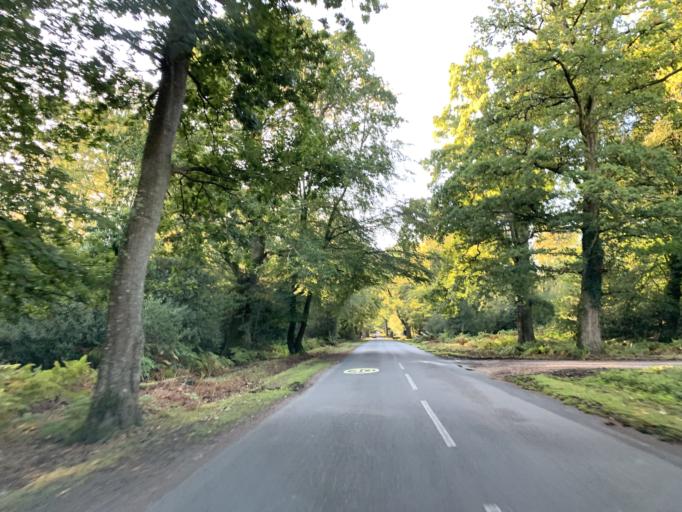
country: GB
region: England
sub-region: Hampshire
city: West Wellow
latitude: 50.9570
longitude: -1.6303
